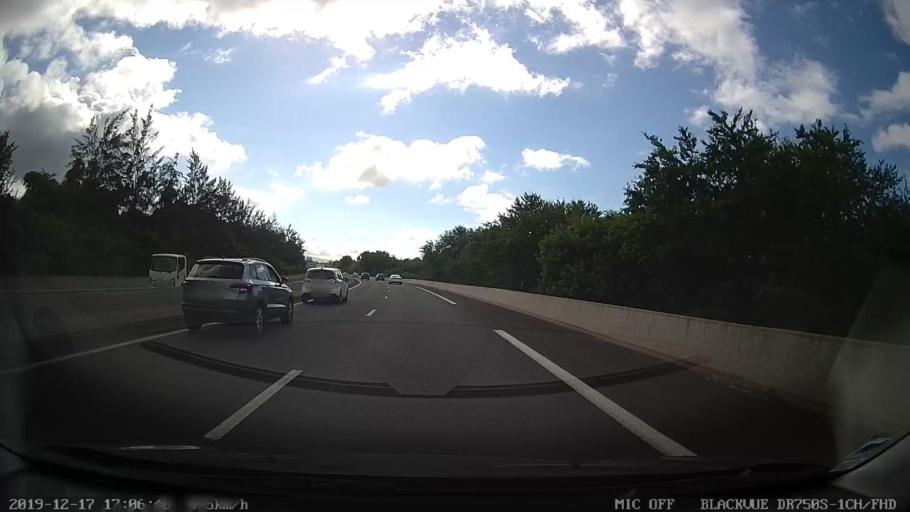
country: RE
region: Reunion
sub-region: Reunion
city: Saint-Louis
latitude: -21.2829
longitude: 55.3683
